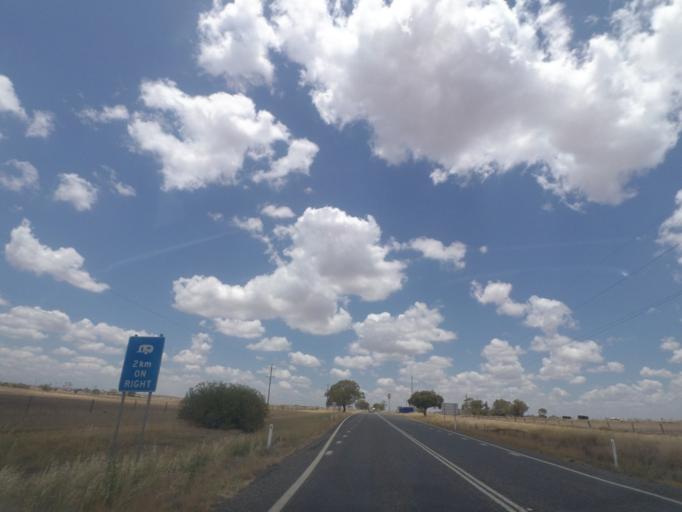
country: AU
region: Queensland
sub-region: Southern Downs
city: Warwick
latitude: -27.9305
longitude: 151.9859
